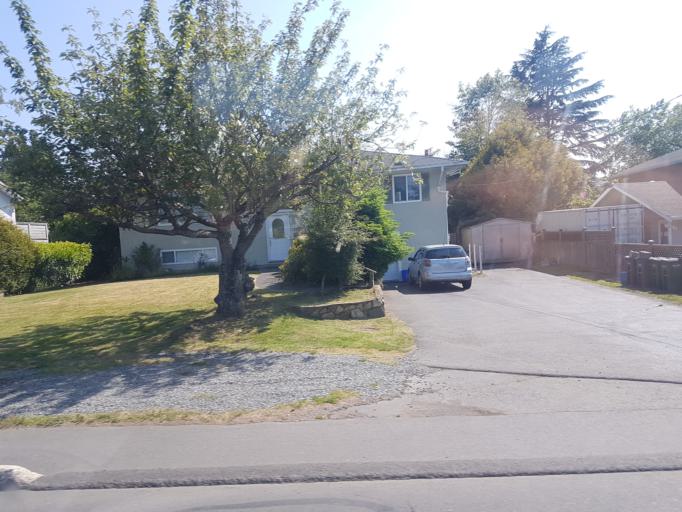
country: CA
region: British Columbia
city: Oak Bay
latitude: 48.4922
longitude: -123.3281
